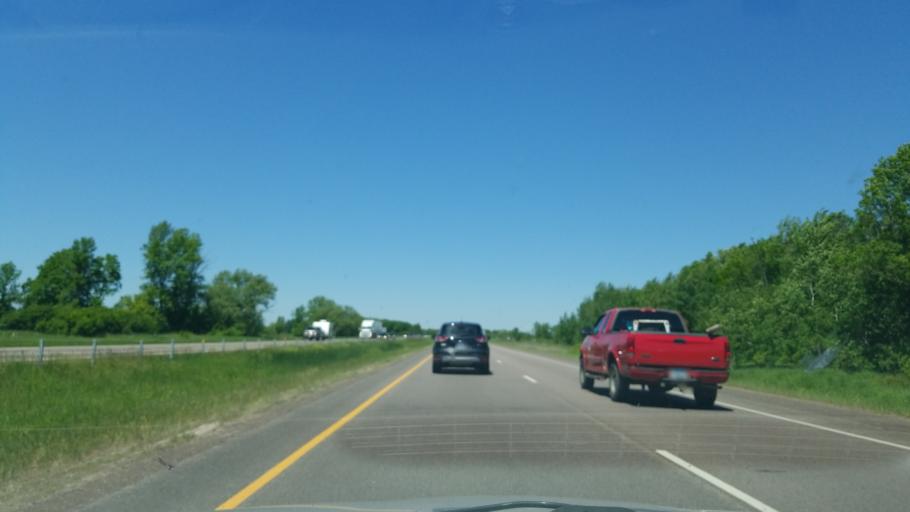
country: US
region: Minnesota
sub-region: Chisago County
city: Rush City
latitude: 45.6904
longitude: -92.9909
